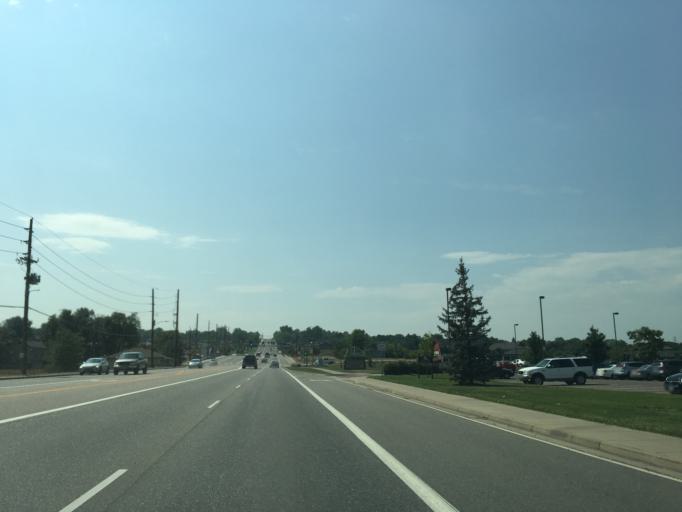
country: US
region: Colorado
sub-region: Jefferson County
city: Wheat Ridge
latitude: 39.7729
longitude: -105.1098
